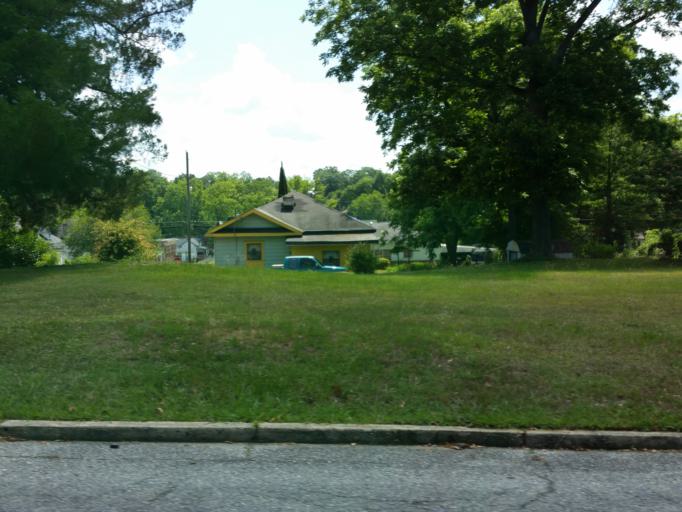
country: US
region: Mississippi
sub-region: Lauderdale County
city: Meridian
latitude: 32.3676
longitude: -88.7137
